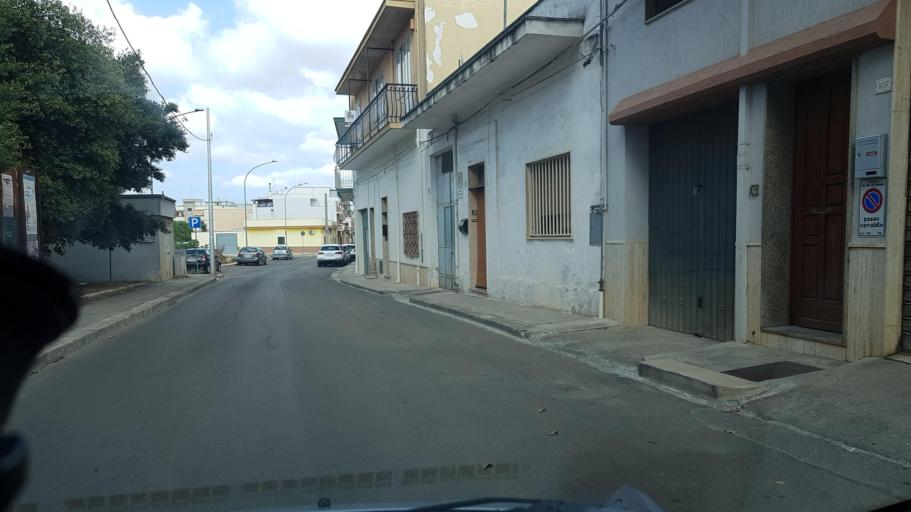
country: IT
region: Apulia
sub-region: Provincia di Brindisi
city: San Vito dei Normanni
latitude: 40.6563
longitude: 17.7145
